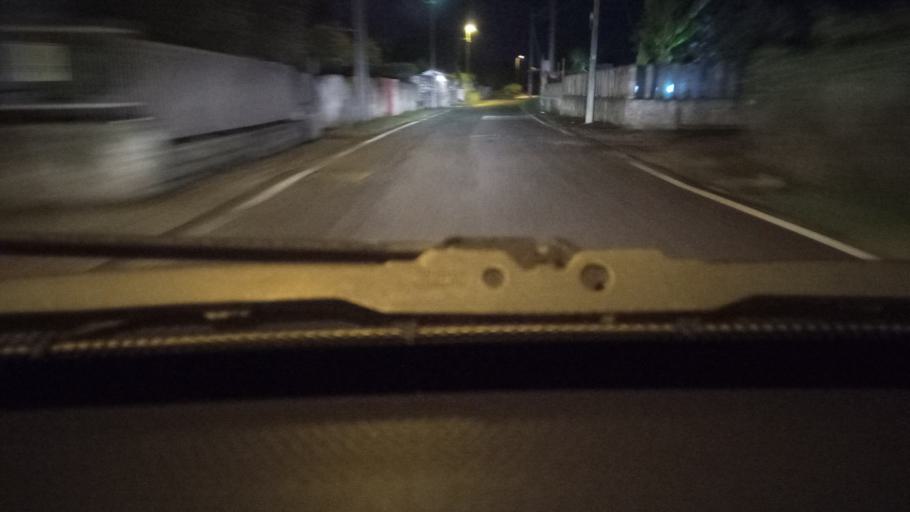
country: IT
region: Latium
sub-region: Provincia di Latina
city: Minturno
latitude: 41.2425
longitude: 13.7389
